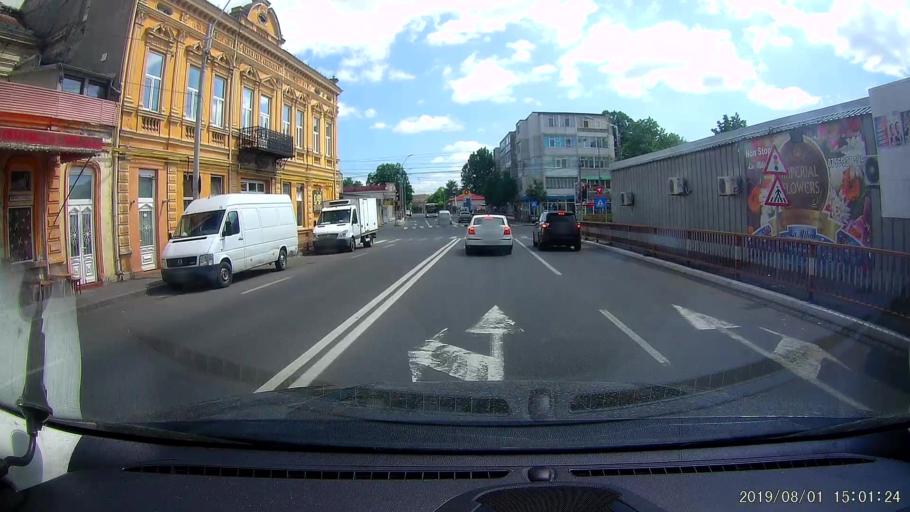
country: RO
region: Braila
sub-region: Municipiul Braila
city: Braila
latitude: 45.2718
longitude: 27.9603
